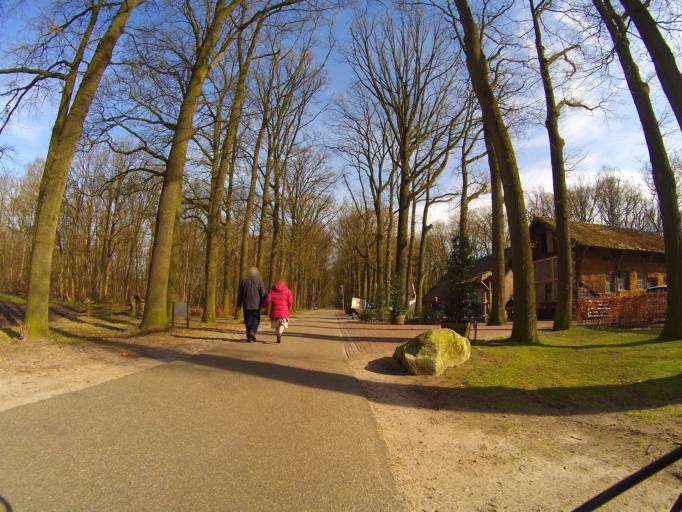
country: NL
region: Utrecht
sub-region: Gemeente Baarn
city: Baarn
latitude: 52.2163
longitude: 5.2552
